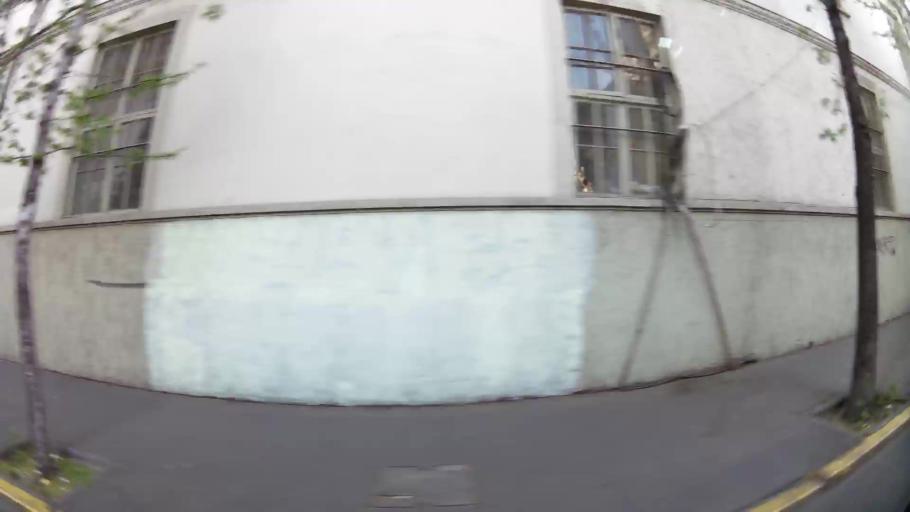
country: CL
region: Santiago Metropolitan
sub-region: Provincia de Santiago
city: Santiago
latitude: -33.4457
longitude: -70.6427
